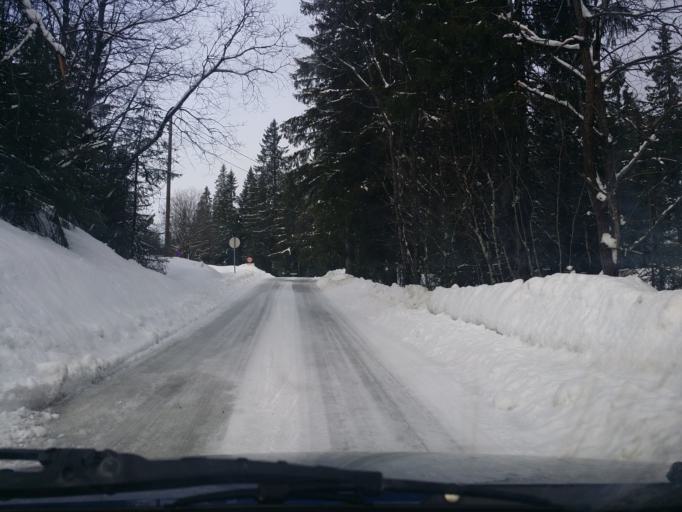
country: NO
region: Buskerud
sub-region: Lier
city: Lierbyen
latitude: 59.8215
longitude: 10.1726
